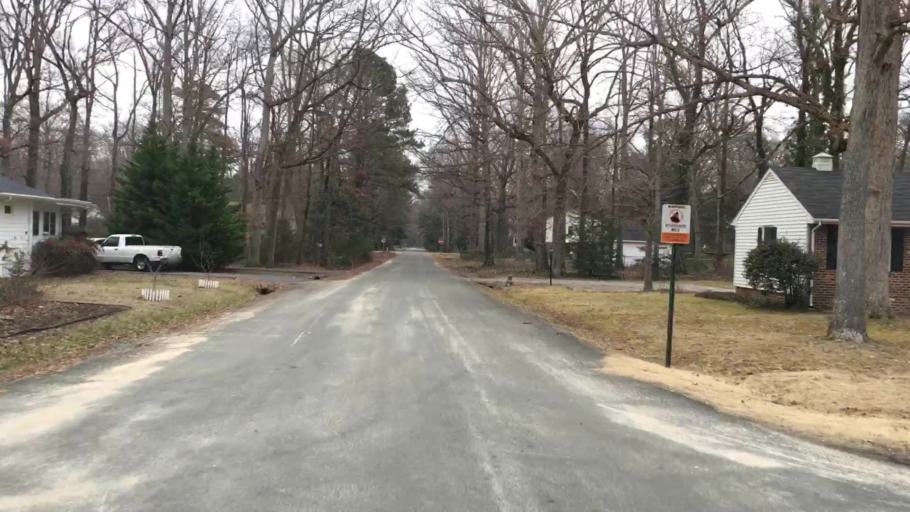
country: US
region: Virginia
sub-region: Chesterfield County
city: Bon Air
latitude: 37.5371
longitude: -77.5772
